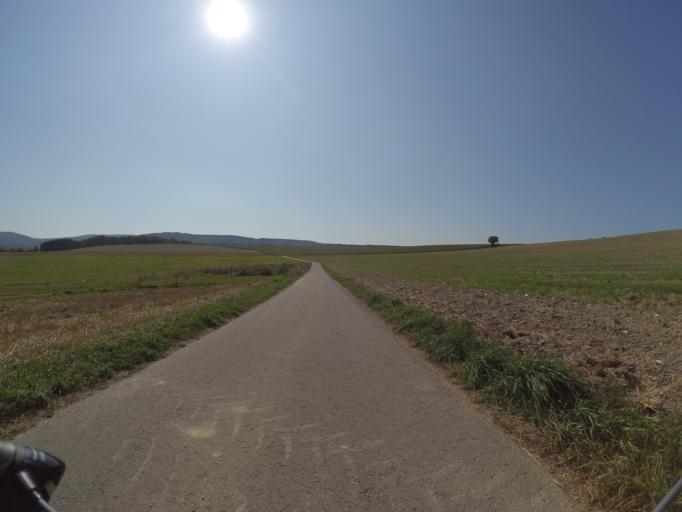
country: DE
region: Rheinland-Pfalz
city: Deuselbach
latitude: 49.7576
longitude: 7.0436
